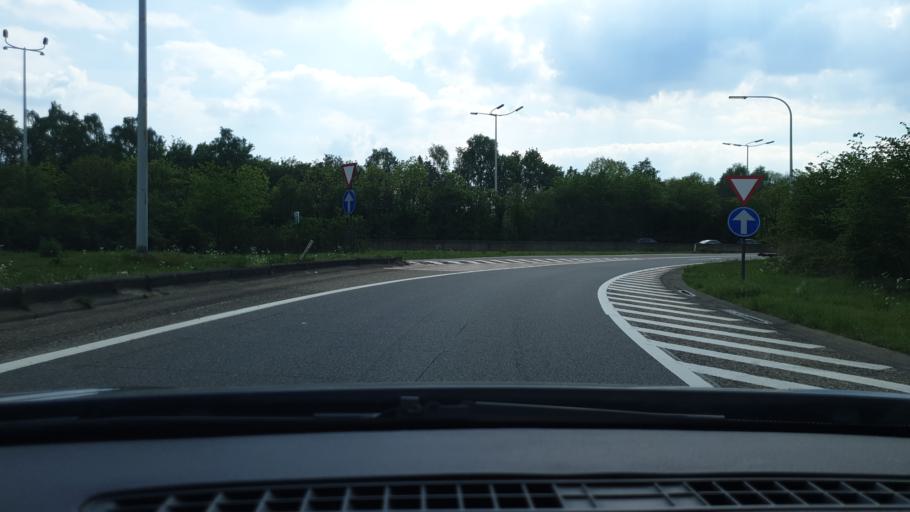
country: BE
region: Flanders
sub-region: Provincie Limburg
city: Houthalen
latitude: 51.0130
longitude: 5.3765
